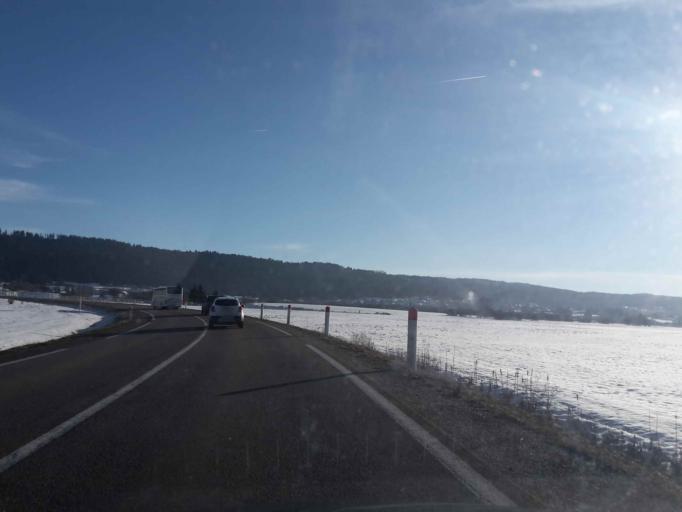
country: FR
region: Franche-Comte
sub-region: Departement du Doubs
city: Pontarlier
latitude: 46.9030
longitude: 6.3296
